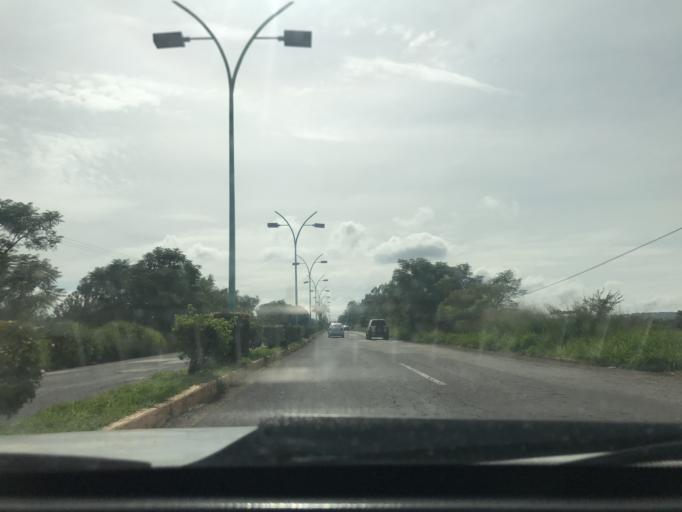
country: MX
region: Morelos
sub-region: Atlatlahucan
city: Colonia San Francisco
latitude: 18.8948
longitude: -98.9024
